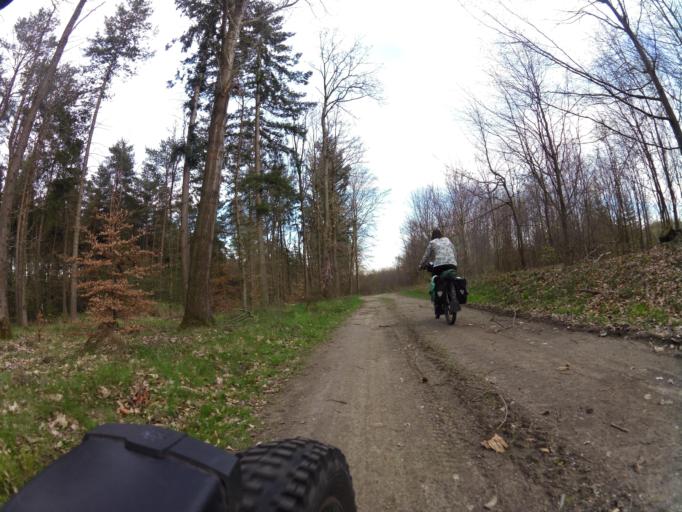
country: PL
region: West Pomeranian Voivodeship
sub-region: Powiat lobeski
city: Lobez
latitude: 53.7428
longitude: 15.6264
